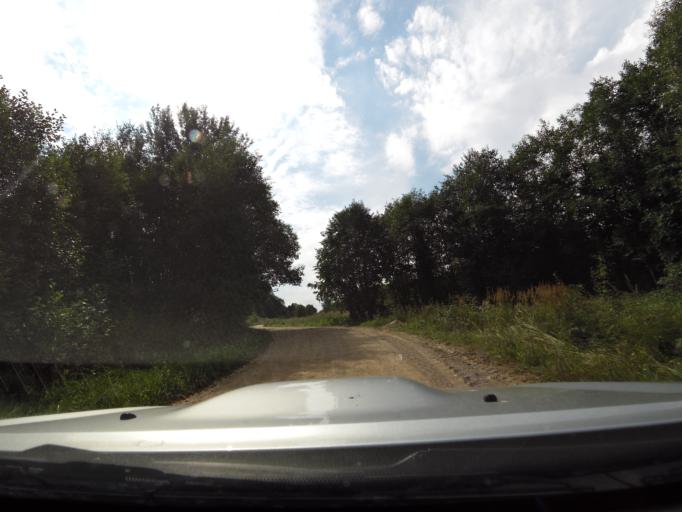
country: LT
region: Vilnius County
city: Elektrenai
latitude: 54.9198
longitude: 24.7393
